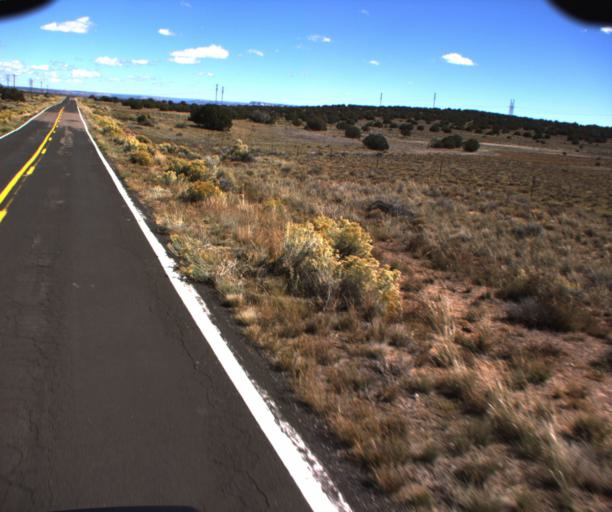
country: US
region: New Mexico
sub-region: McKinley County
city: Zuni Pueblo
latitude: 35.0154
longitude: -109.0570
